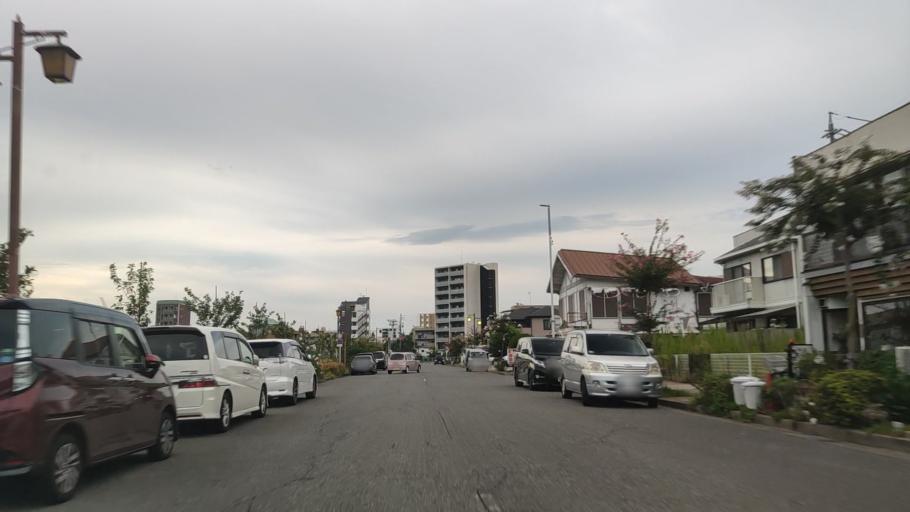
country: JP
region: Aichi
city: Nagoya-shi
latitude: 35.1875
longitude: 136.8979
